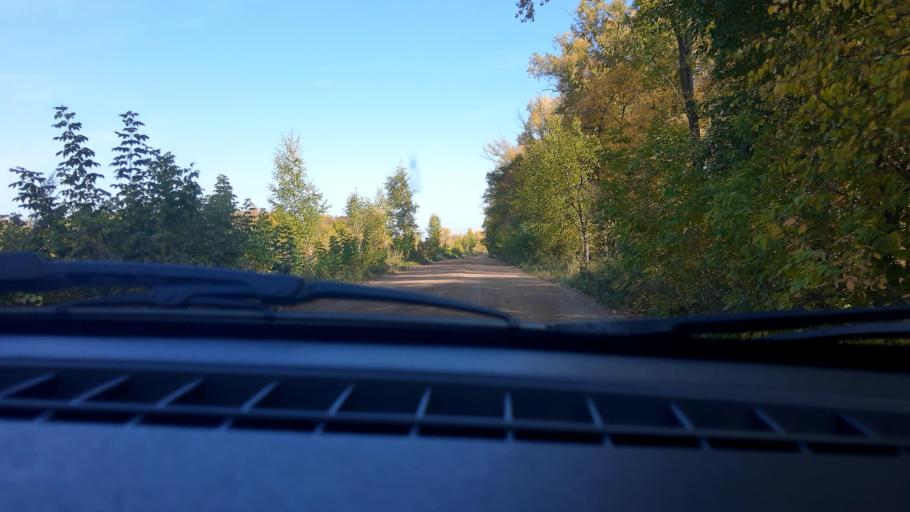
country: RU
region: Bashkortostan
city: Mikhaylovka
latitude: 54.7423
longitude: 55.8559
